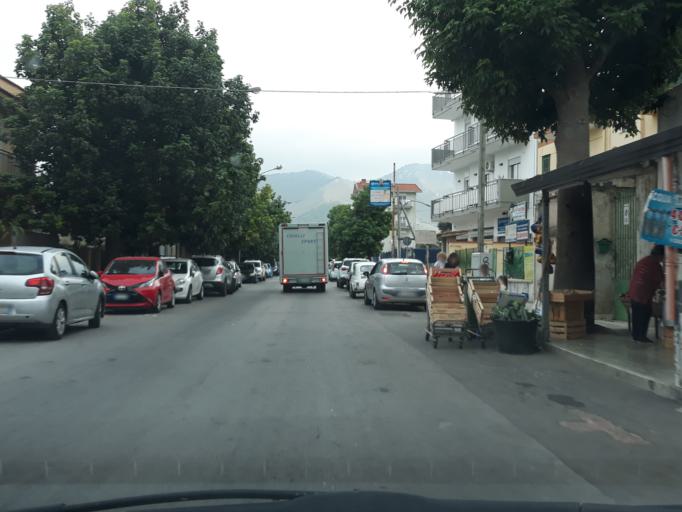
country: IT
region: Sicily
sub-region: Palermo
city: Monreale
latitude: 38.0949
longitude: 13.3193
